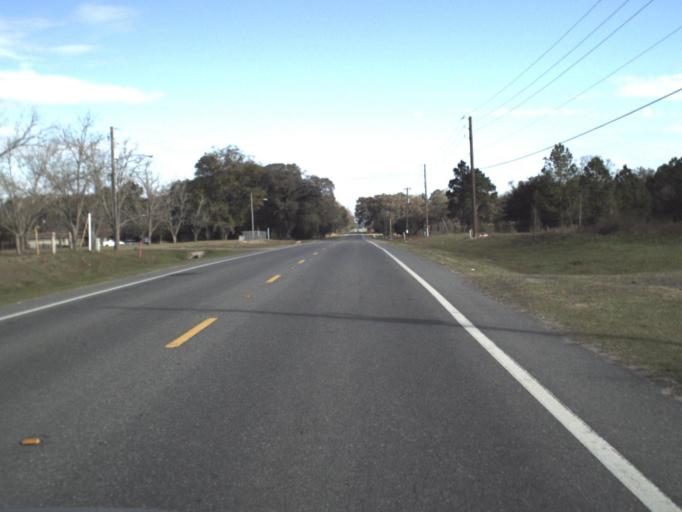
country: US
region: Florida
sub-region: Jackson County
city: Malone
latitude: 30.8871
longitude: -85.1613
